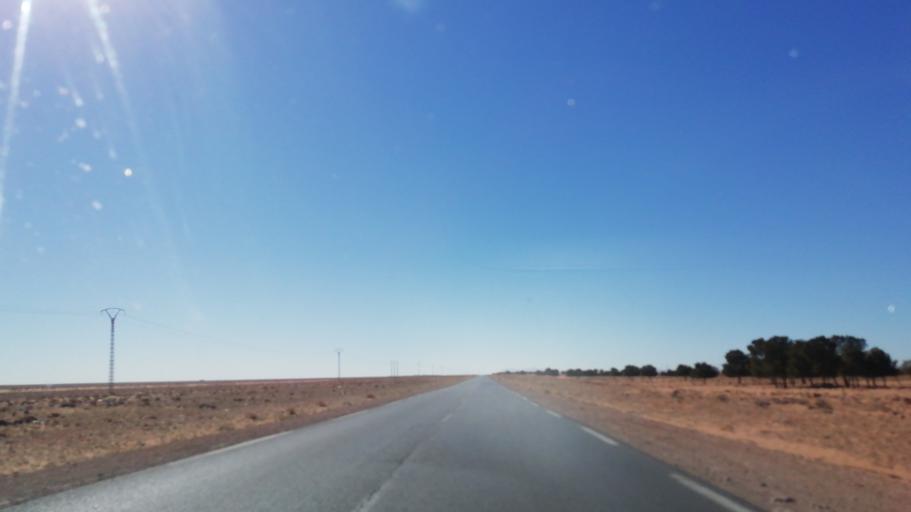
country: DZ
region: Saida
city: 'Ain el Hadjar
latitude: 33.9906
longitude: 0.0357
